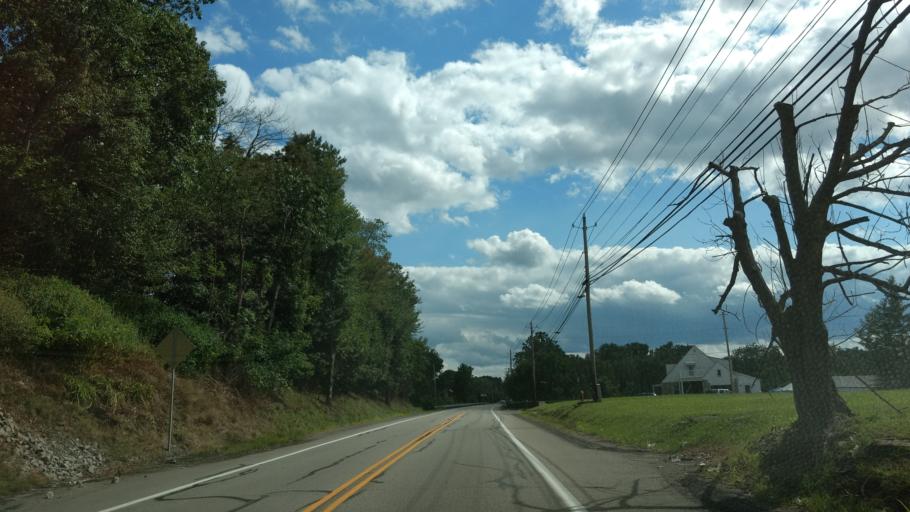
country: US
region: Pennsylvania
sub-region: Armstrong County
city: Apollo
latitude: 40.5394
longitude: -79.5925
